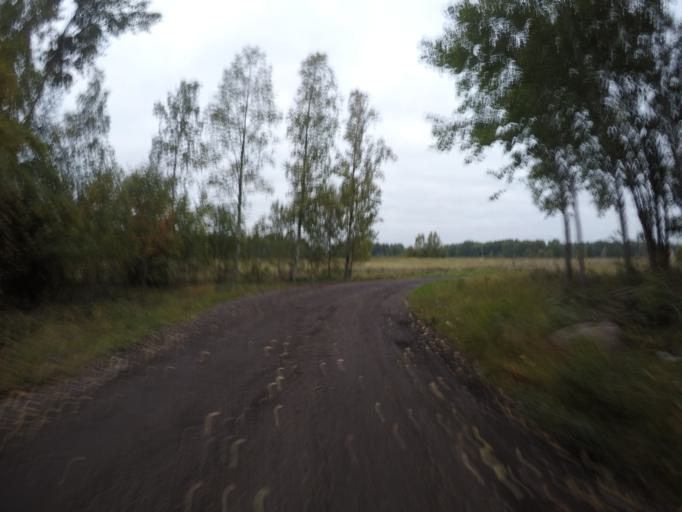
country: SE
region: Vaestmanland
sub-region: Kungsors Kommun
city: Kungsoer
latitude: 59.3995
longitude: 16.1155
